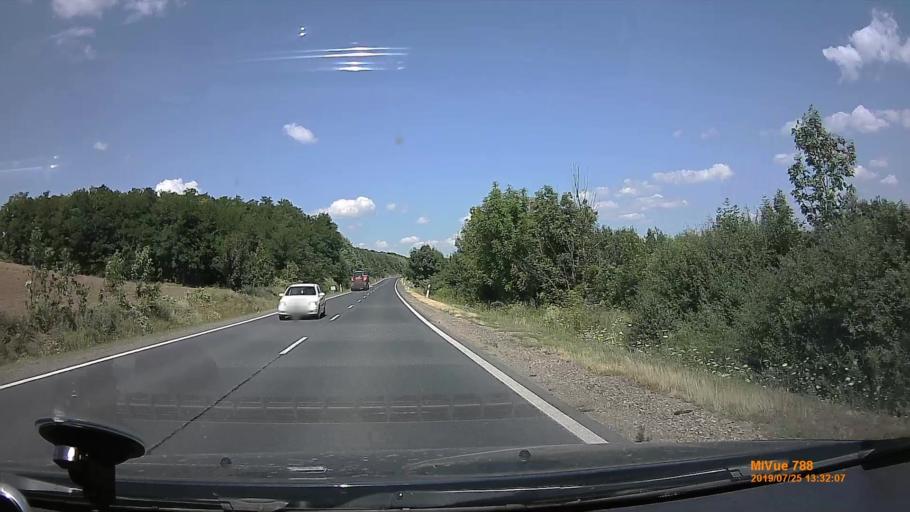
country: HU
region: Borsod-Abauj-Zemplen
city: Encs
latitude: 48.3723
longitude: 21.1437
